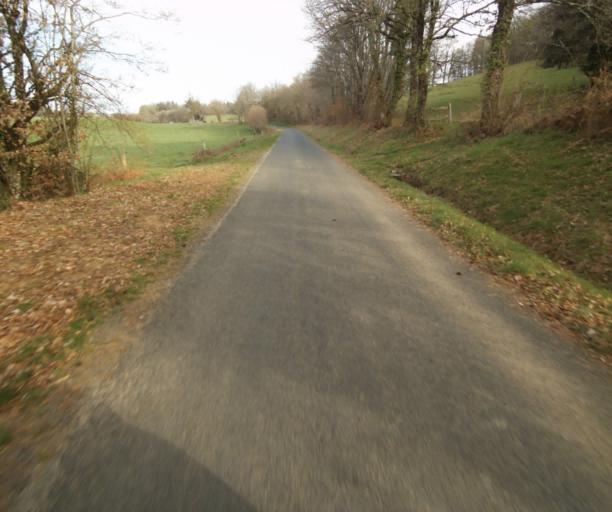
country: FR
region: Limousin
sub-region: Departement de la Correze
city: Chamboulive
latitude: 45.4468
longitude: 1.7559
